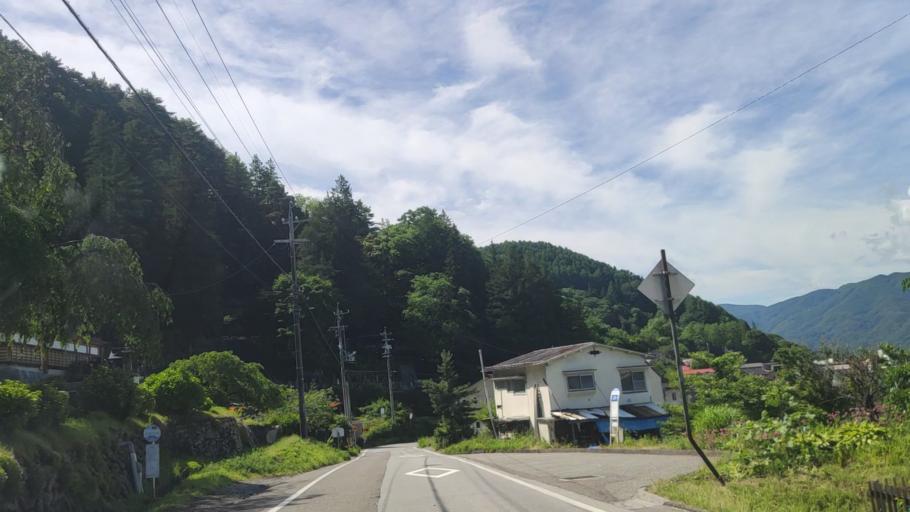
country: JP
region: Nagano
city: Suwa
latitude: 36.0431
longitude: 138.1262
